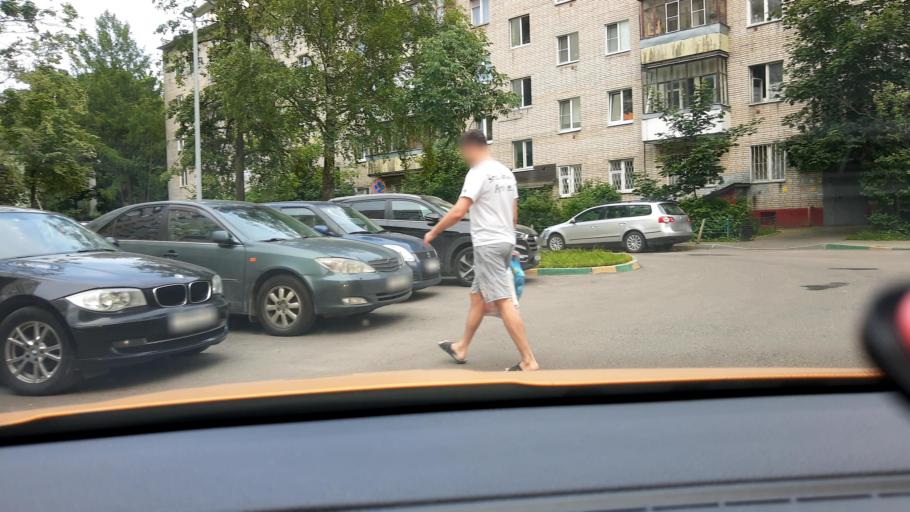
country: RU
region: Moskovskaya
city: Mosrentgen
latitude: 55.6217
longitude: 37.4751
